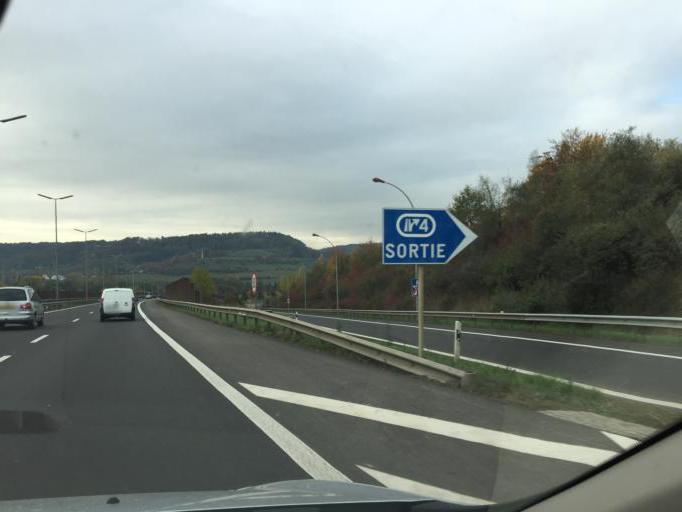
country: LU
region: Luxembourg
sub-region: Canton de Mersch
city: Mersch
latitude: 49.7552
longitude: 6.0917
